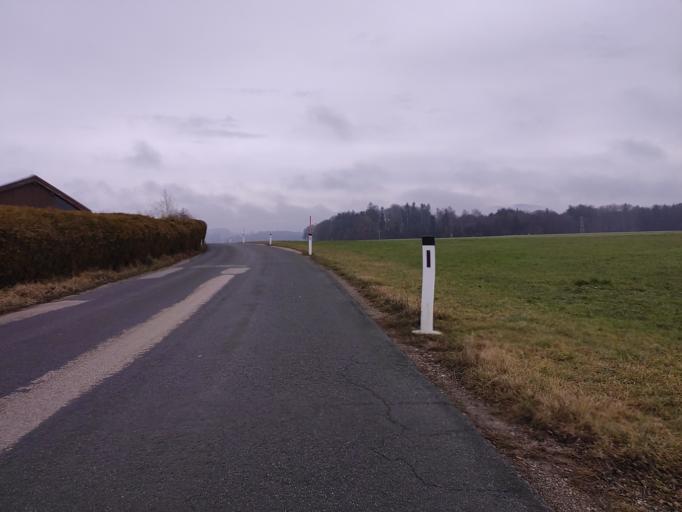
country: AT
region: Salzburg
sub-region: Politischer Bezirk Salzburg-Umgebung
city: Seekirchen am Wallersee
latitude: 47.8939
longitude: 13.1404
